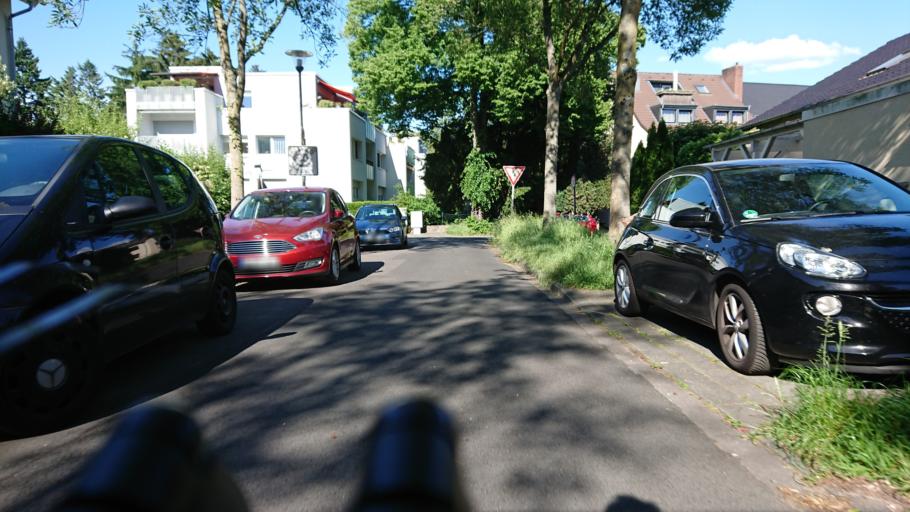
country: DE
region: North Rhine-Westphalia
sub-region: Regierungsbezirk Koln
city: Mengenich
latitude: 50.9431
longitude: 6.8737
